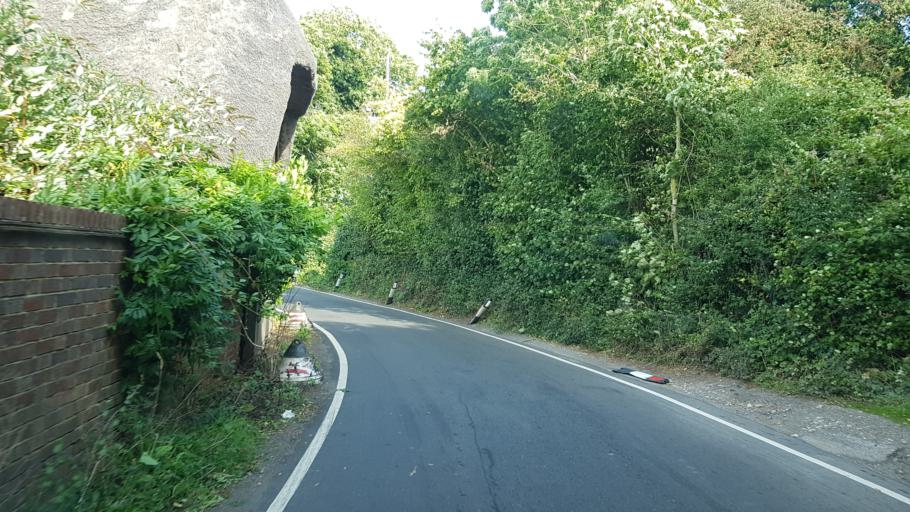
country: GB
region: England
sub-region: Kent
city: Yalding
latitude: 51.2417
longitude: 0.4663
